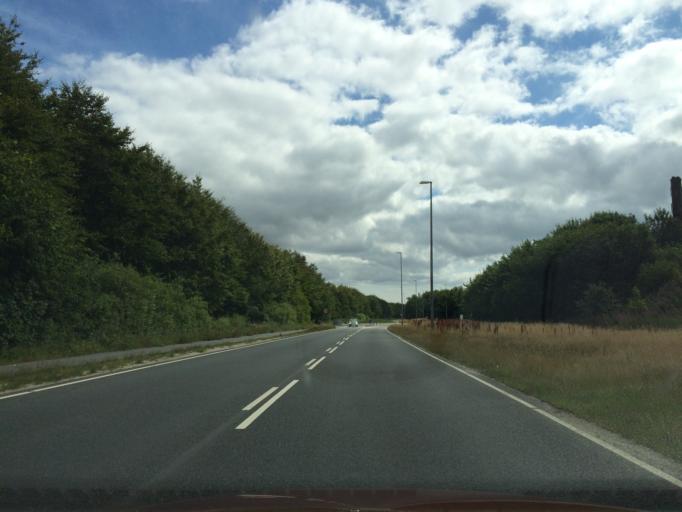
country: DK
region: Central Jutland
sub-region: Silkeborg Kommune
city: Silkeborg
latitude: 56.1960
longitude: 9.5999
